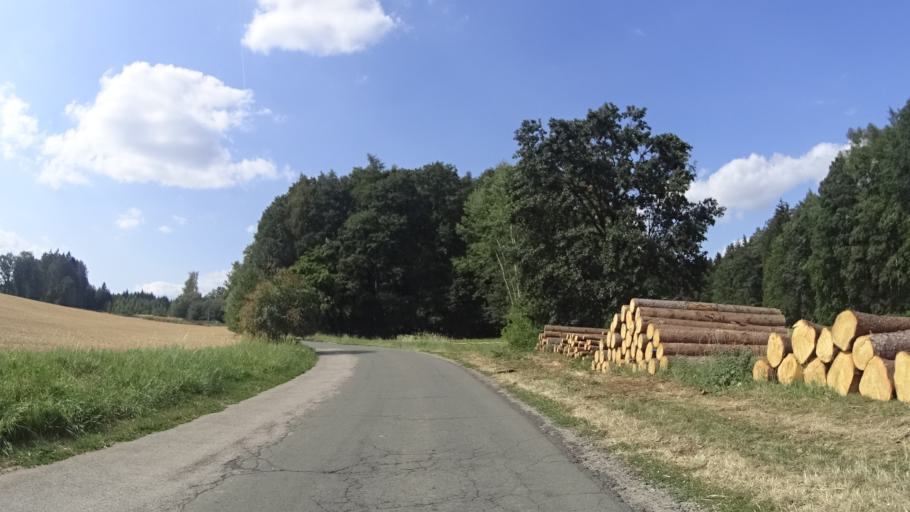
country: CZ
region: Kralovehradecky
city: Liban
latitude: 50.4273
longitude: 15.2596
